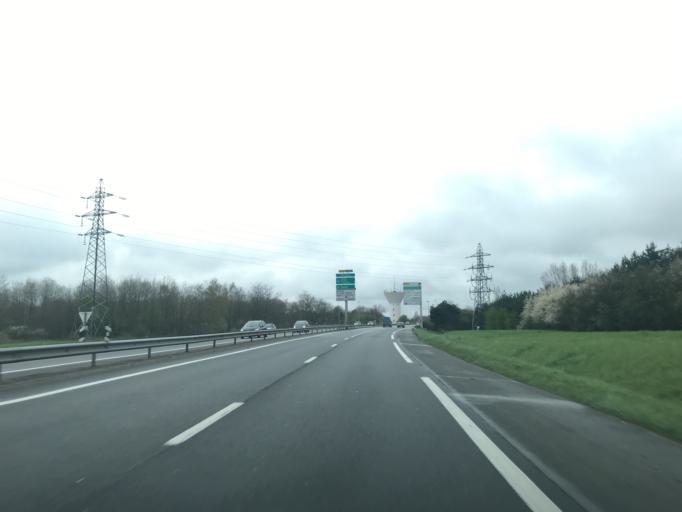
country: FR
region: Centre
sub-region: Departement du Loiret
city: Saint-Jean-de-Braye
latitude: 47.9211
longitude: 1.9978
